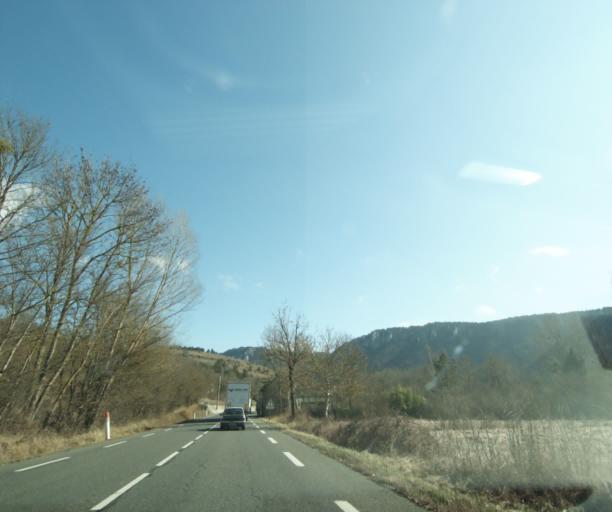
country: FR
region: Languedoc-Roussillon
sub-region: Departement de la Lozere
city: Chanac
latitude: 44.4890
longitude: 3.3771
